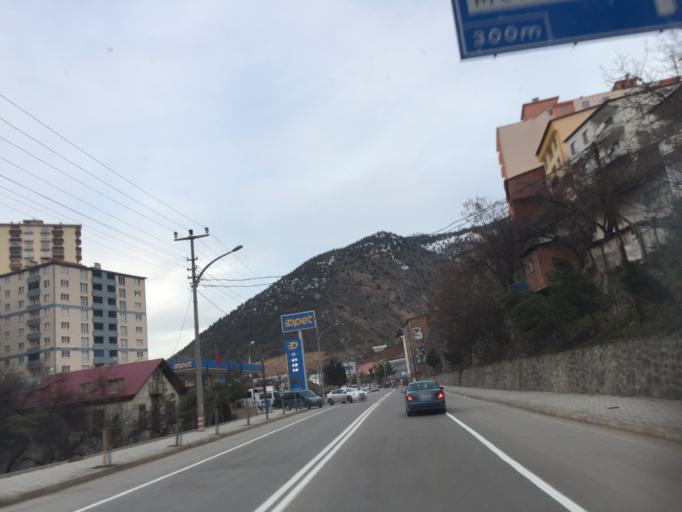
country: TR
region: Gumushane
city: Gumushkhane
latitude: 40.4639
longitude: 39.4650
